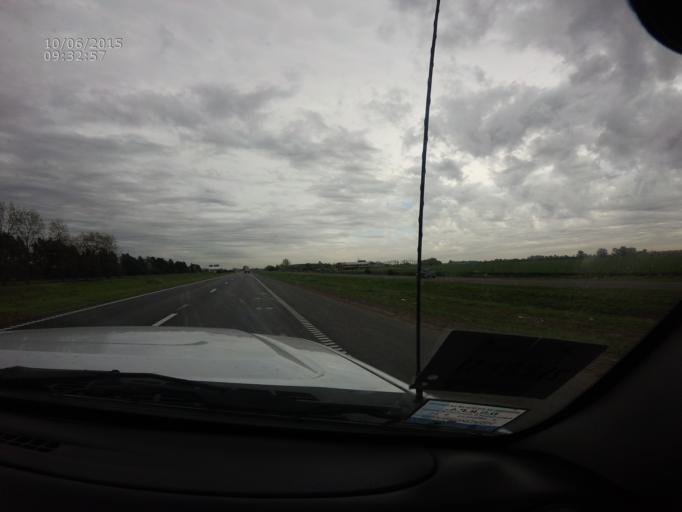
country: AR
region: Buenos Aires
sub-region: Partido de Zarate
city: Zarate
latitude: -34.1231
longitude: -59.0887
